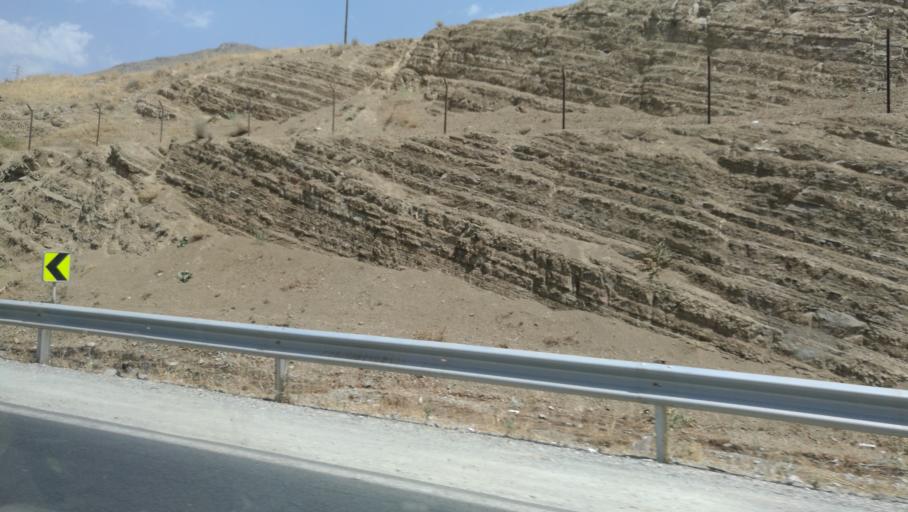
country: IR
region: Alborz
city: Karaj
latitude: 35.8249
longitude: 51.0409
